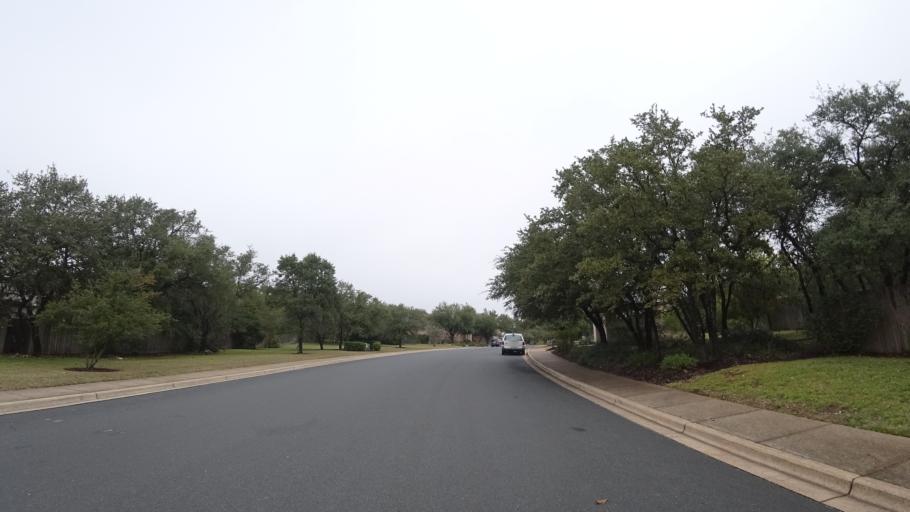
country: US
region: Texas
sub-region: Travis County
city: Shady Hollow
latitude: 30.1923
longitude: -97.8770
